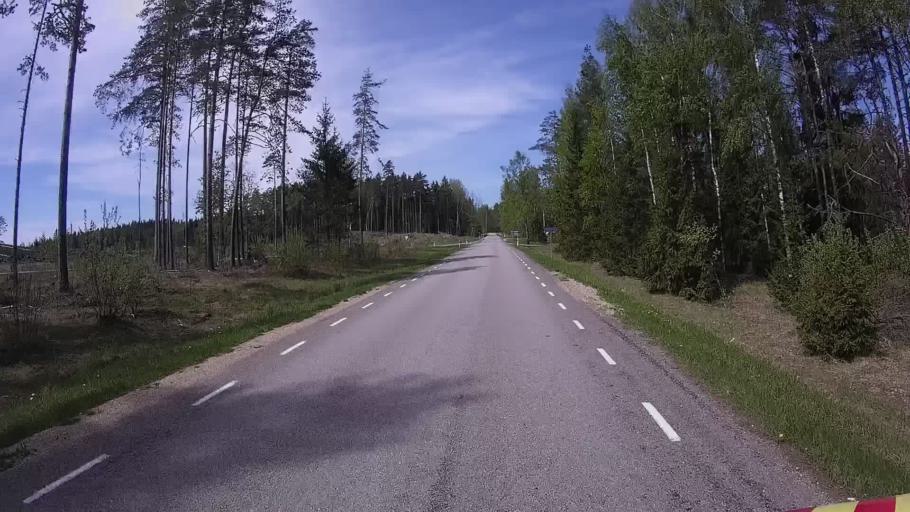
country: EE
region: Vorumaa
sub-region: Antsla vald
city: Vana-Antsla
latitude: 57.6202
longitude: 26.3524
